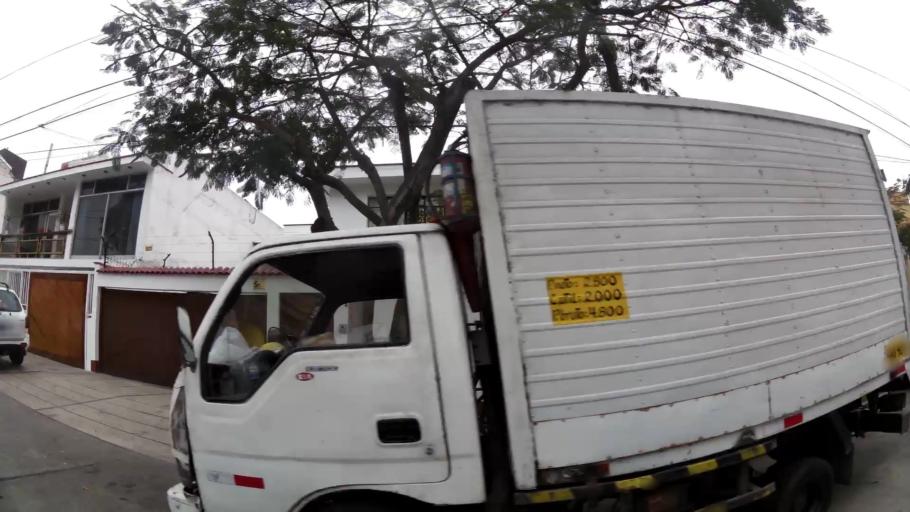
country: PE
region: Lima
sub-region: Lima
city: San Luis
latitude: -12.0997
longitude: -77.0165
